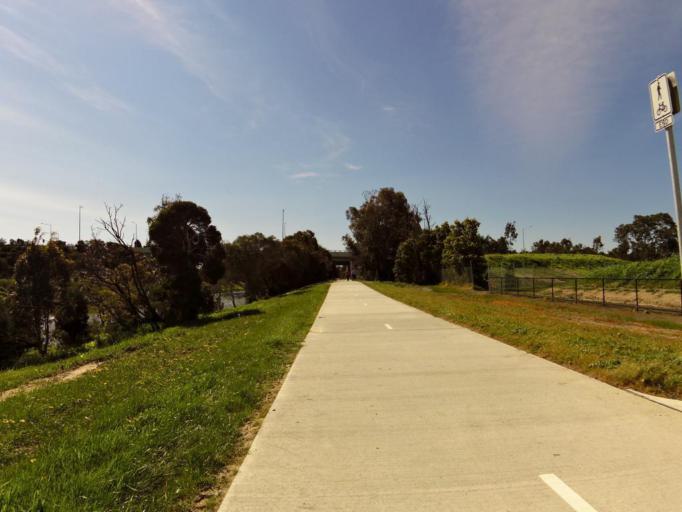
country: AU
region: Victoria
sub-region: Greater Dandenong
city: Dandenong
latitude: -38.0029
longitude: 145.1930
